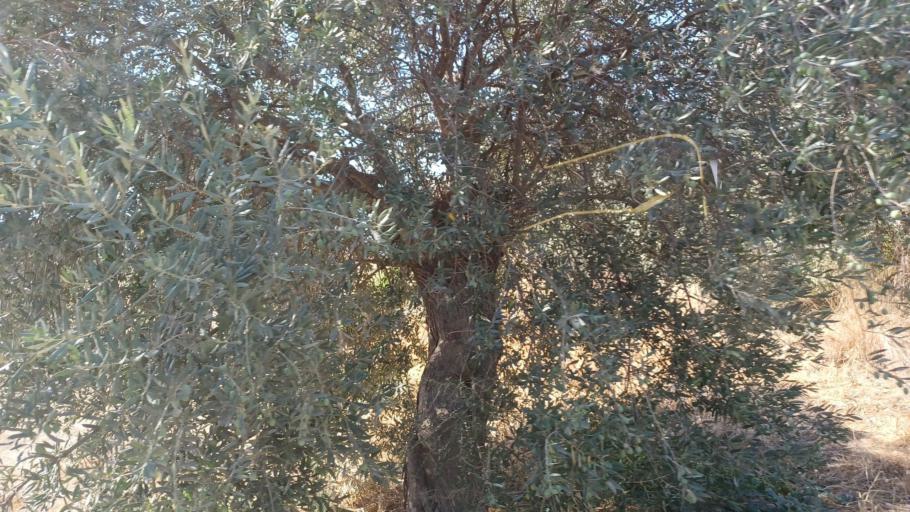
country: CY
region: Pafos
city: Polis
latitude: 35.0353
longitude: 32.4311
